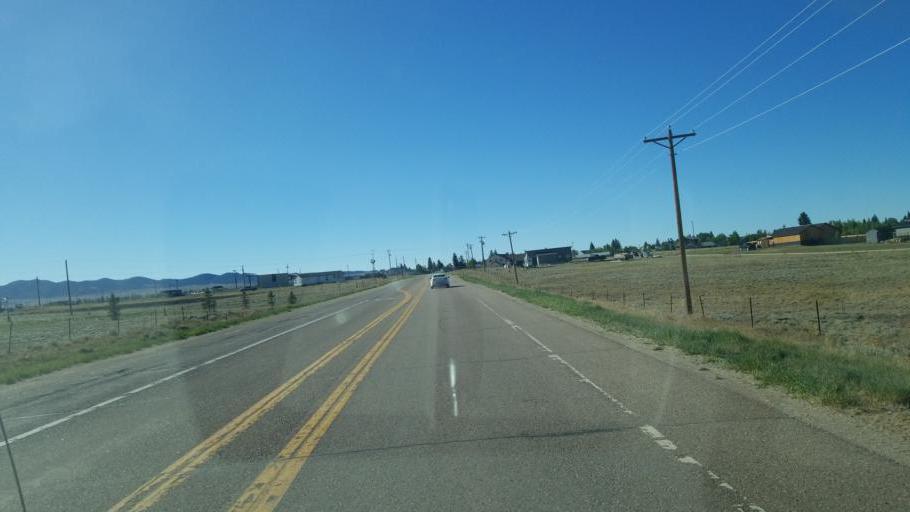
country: US
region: Colorado
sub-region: Custer County
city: Westcliffe
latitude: 38.1415
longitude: -105.4719
